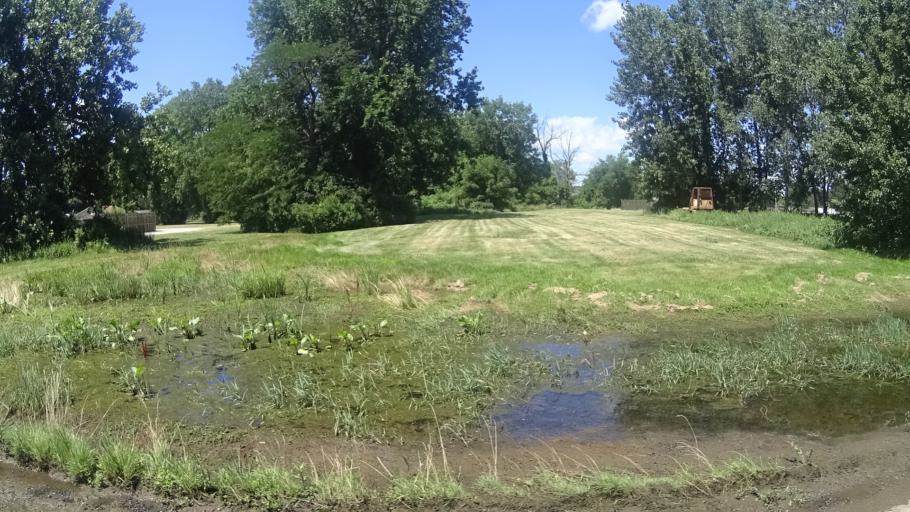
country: US
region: Ohio
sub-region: Erie County
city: Sandusky
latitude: 41.4491
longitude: -82.6708
